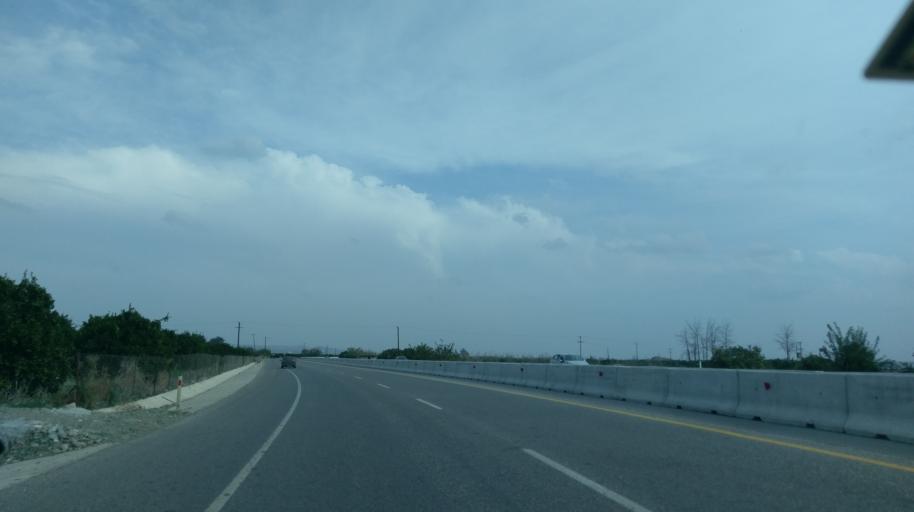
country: CY
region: Lefkosia
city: Morfou
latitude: 35.1973
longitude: 33.0173
